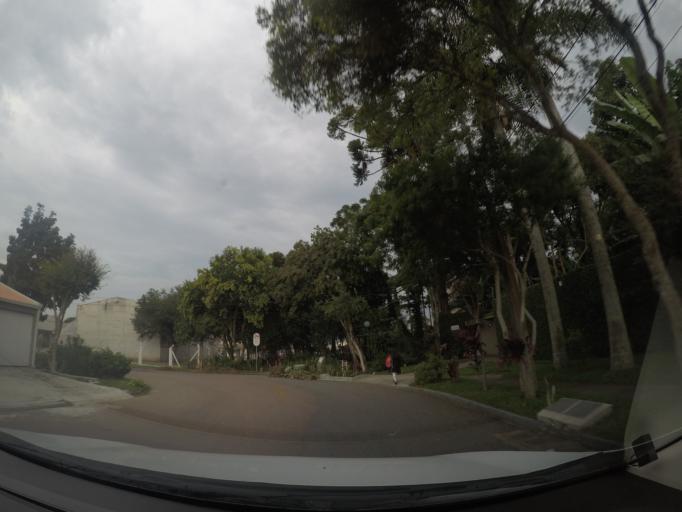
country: BR
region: Parana
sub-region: Sao Jose Dos Pinhais
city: Sao Jose dos Pinhais
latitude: -25.5234
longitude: -49.2351
